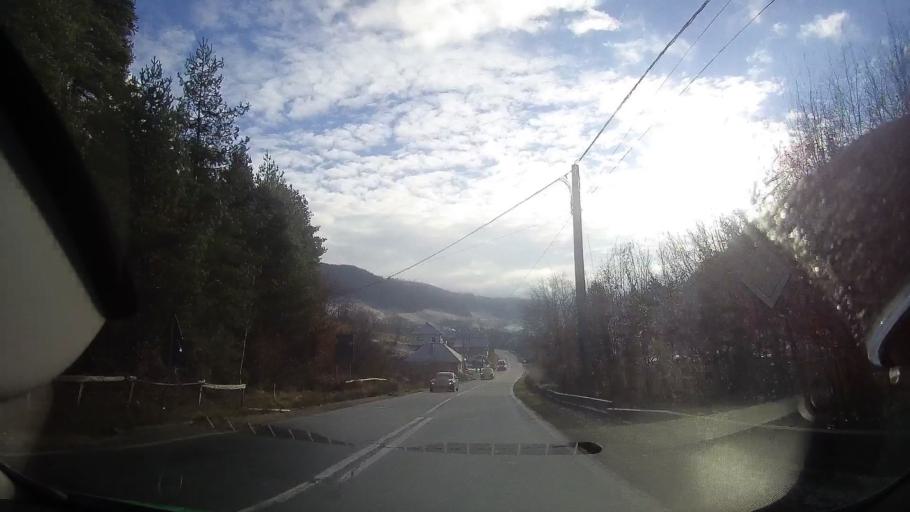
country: RO
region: Alba
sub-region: Comuna Sohodol
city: Sohodol
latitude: 46.3727
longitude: 23.0199
